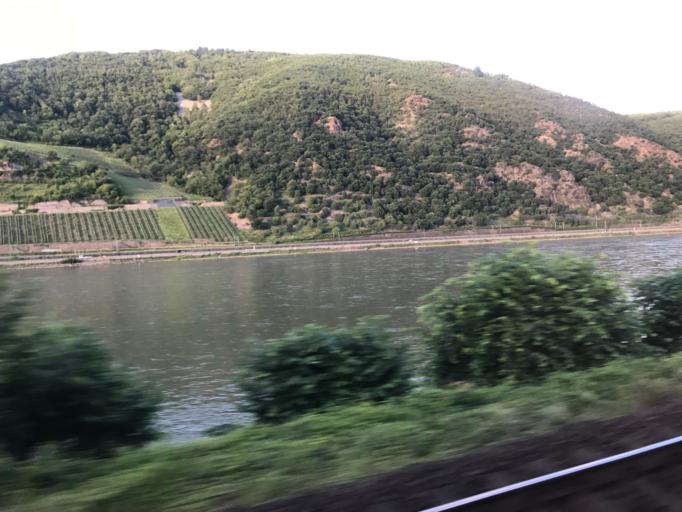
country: DE
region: Rheinland-Pfalz
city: Trechtingshausen
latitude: 50.0112
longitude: 7.8507
